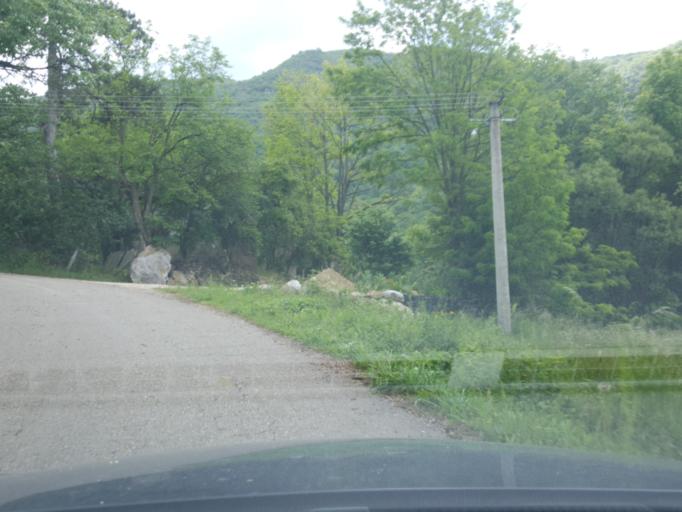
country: RS
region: Central Serbia
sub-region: Zajecarski Okrug
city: Soko Banja
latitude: 43.6324
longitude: 21.9902
